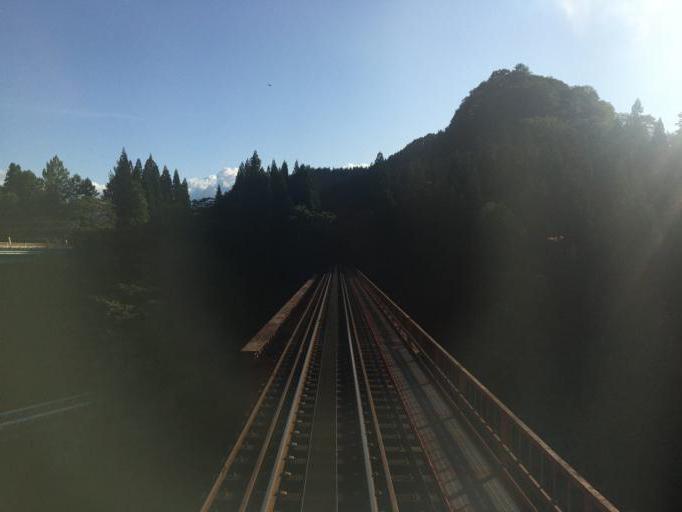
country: JP
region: Akita
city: Takanosu
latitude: 39.9534
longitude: 140.4153
